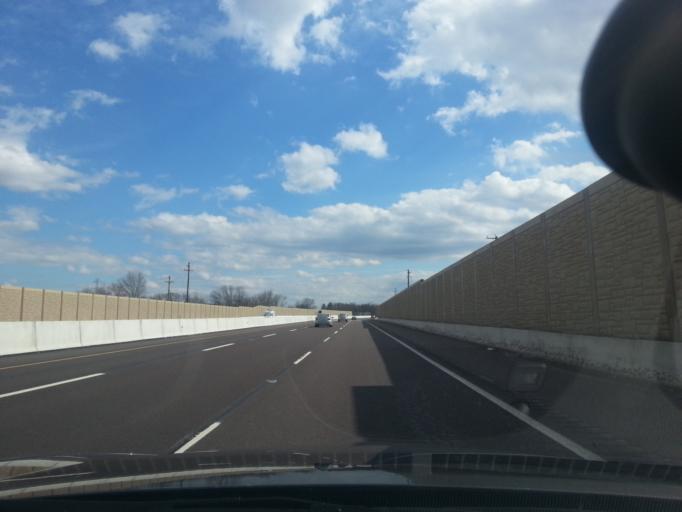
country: US
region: Pennsylvania
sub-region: Montgomery County
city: Blue Bell
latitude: 40.1556
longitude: -75.2952
